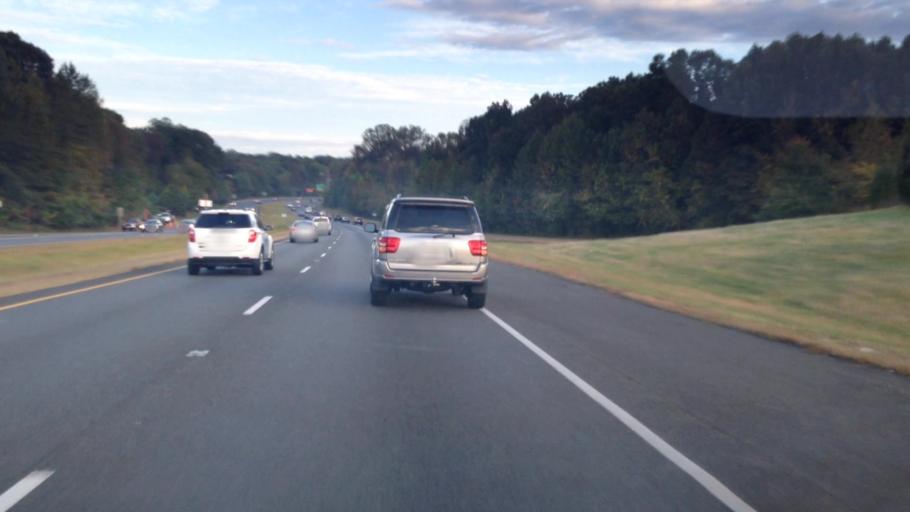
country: US
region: Virginia
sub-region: Fairfax County
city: Fairfax Station
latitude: 38.8300
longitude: -77.3676
